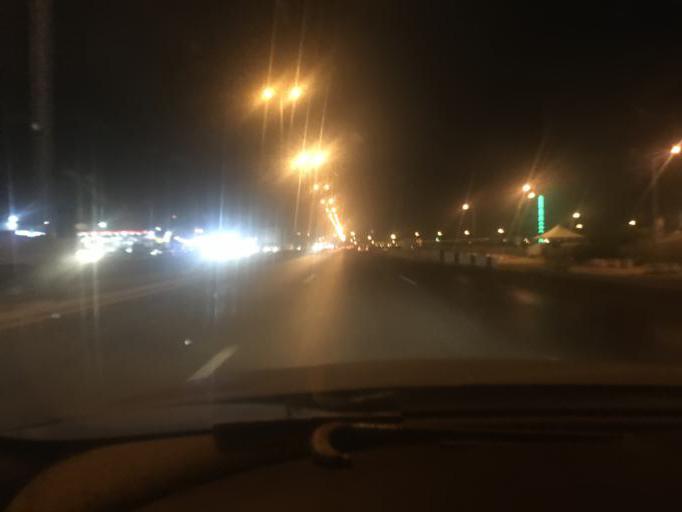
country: SA
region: Ar Riyad
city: Riyadh
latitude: 24.8323
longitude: 46.7315
